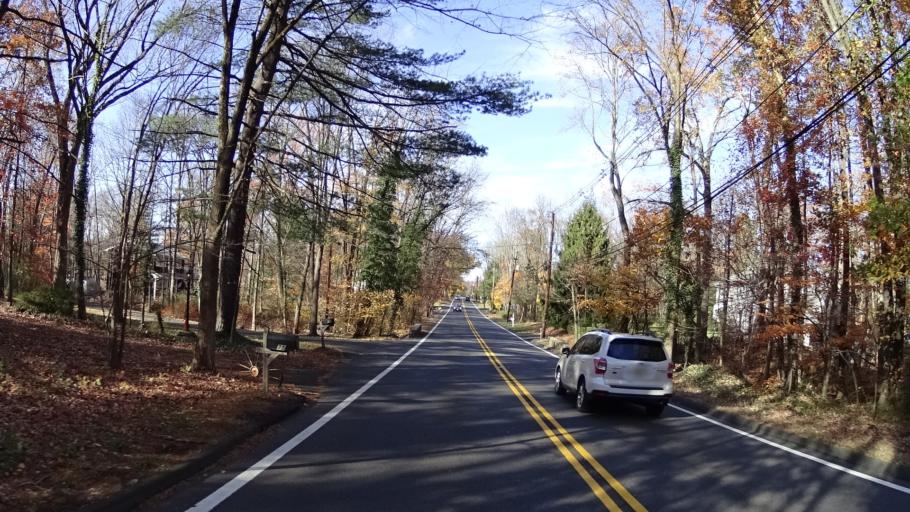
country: US
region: New Jersey
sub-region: Union County
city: Berkeley Heights
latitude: 40.6628
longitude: -74.4572
